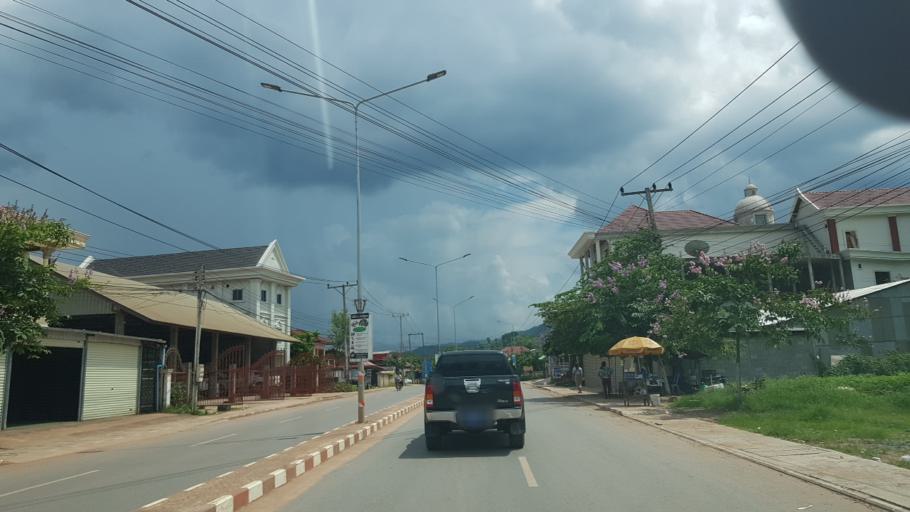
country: LA
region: Oudomxai
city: Muang Xay
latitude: 20.6765
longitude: 101.9860
